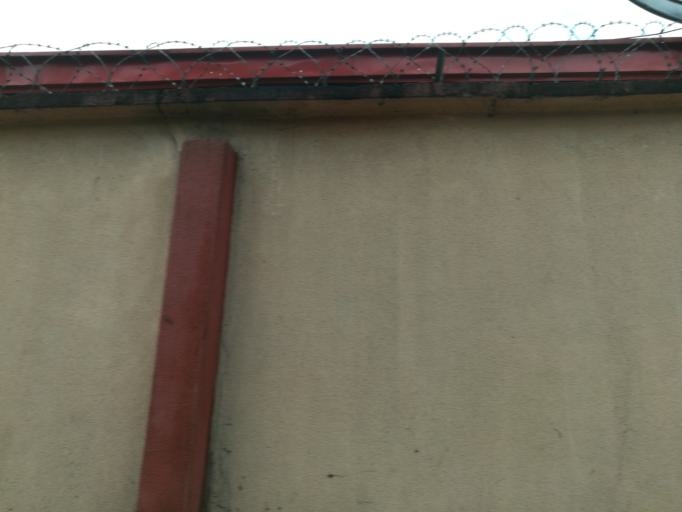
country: NG
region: Rivers
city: Port Harcourt
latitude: 4.8625
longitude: 7.0421
